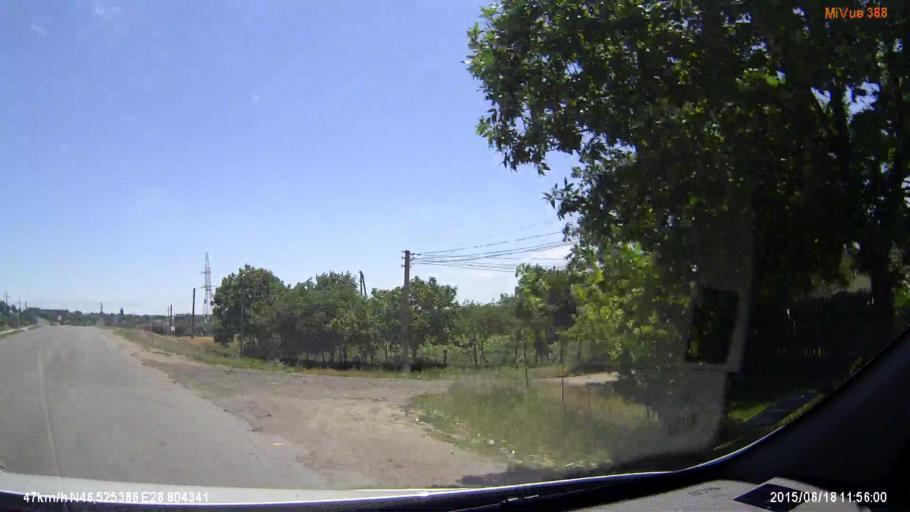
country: MD
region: Cimislia
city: Cimislia
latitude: 46.5254
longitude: 28.8038
